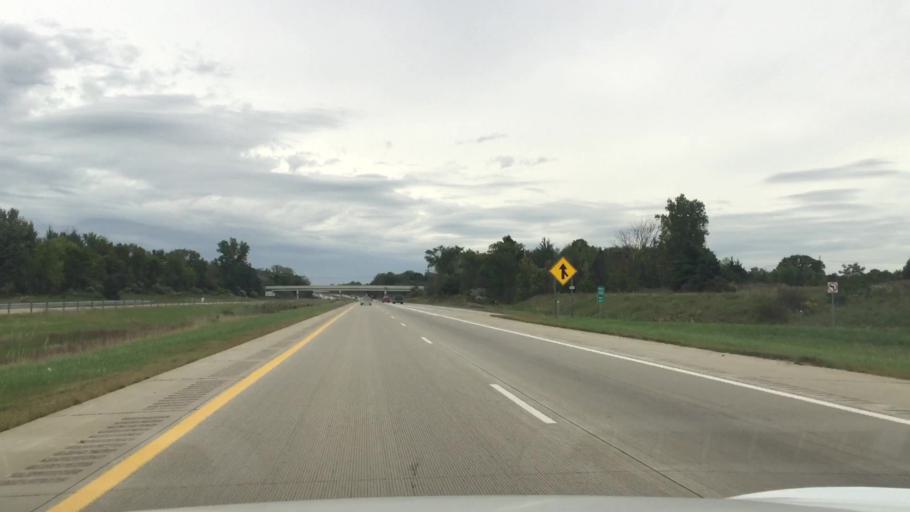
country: US
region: Michigan
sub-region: Macomb County
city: Richmond
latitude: 42.8117
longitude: -82.6306
